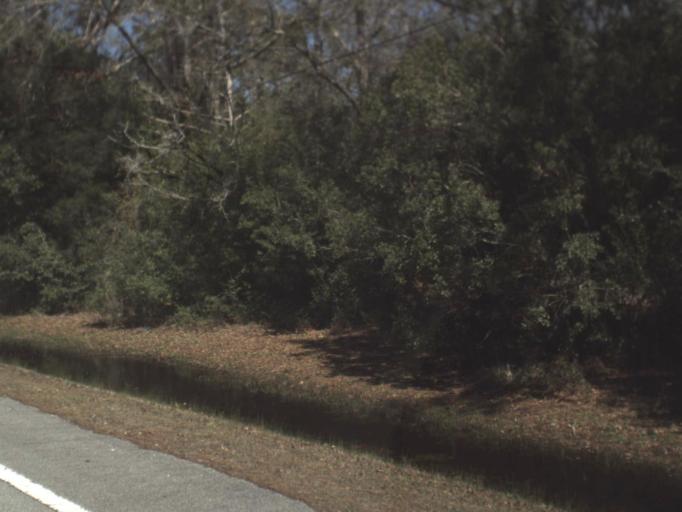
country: US
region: Florida
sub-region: Leon County
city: Woodville
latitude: 30.1833
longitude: -84.2131
